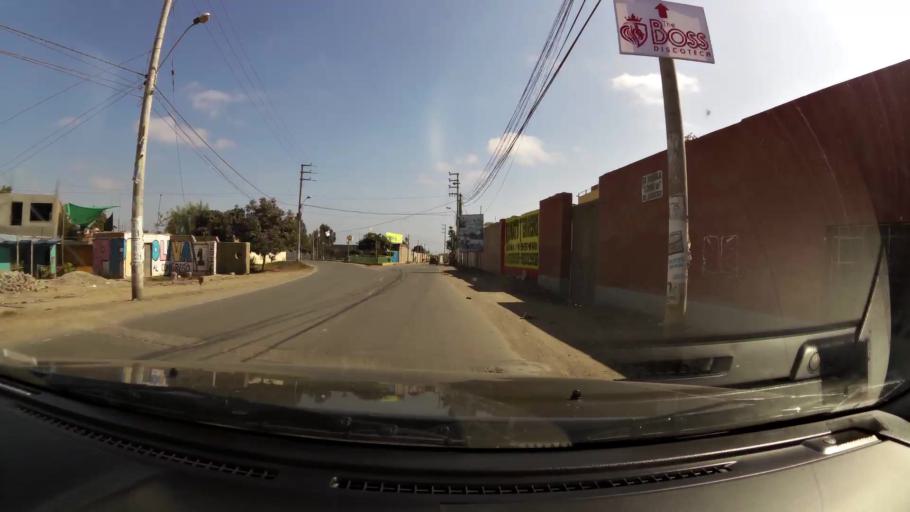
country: PE
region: Ica
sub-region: Provincia de Chincha
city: Sunampe
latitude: -13.4169
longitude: -76.1568
